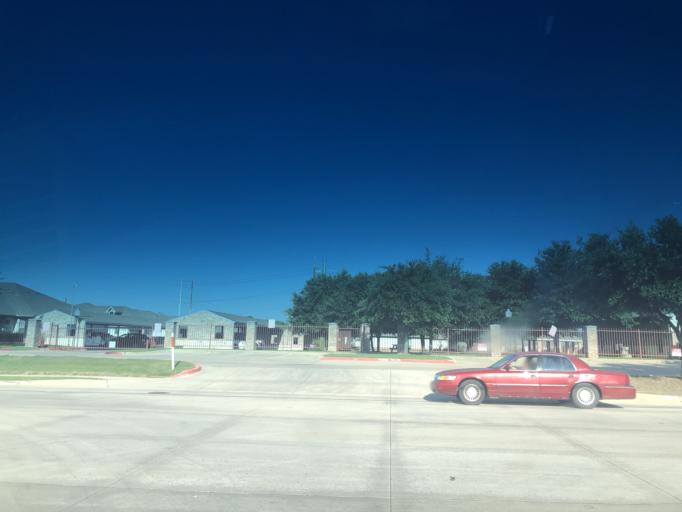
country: US
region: Texas
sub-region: Dallas County
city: Grand Prairie
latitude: 32.7135
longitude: -97.0195
